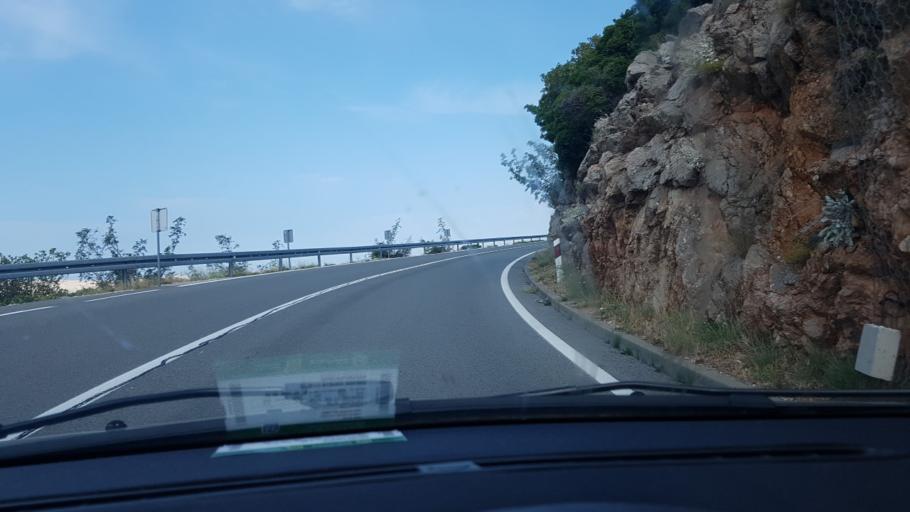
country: HR
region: Zadarska
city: Stari Grad
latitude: 44.4528
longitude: 15.1737
